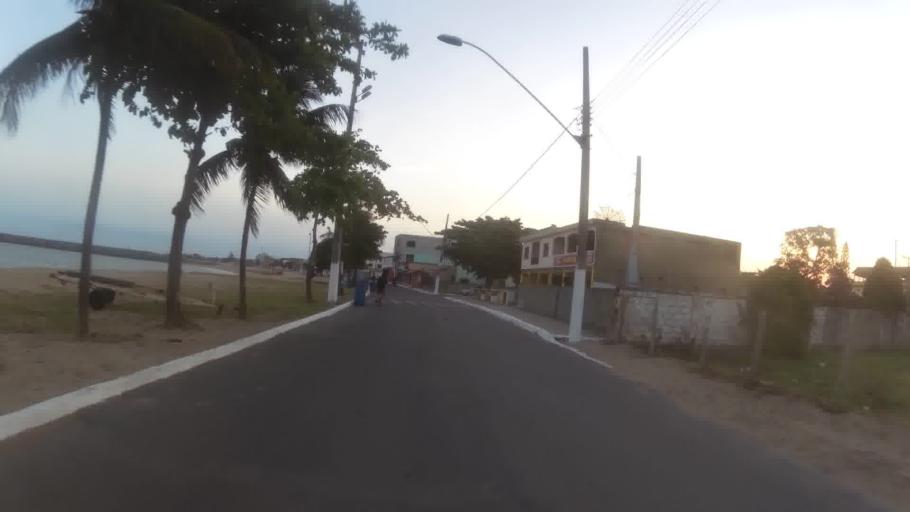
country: BR
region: Espirito Santo
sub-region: Piuma
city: Piuma
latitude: -20.8918
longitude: -40.7727
